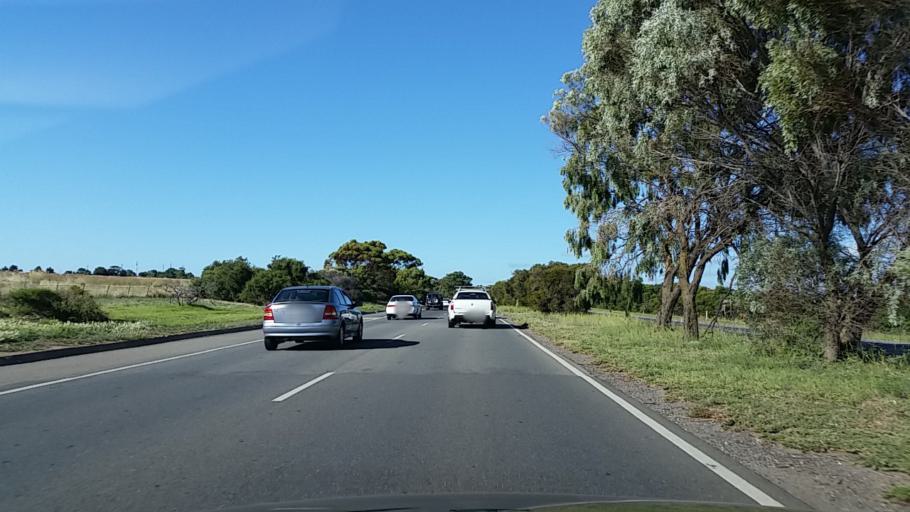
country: AU
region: South Australia
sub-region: Marion
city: Trott Park
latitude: -35.0662
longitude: 138.5316
